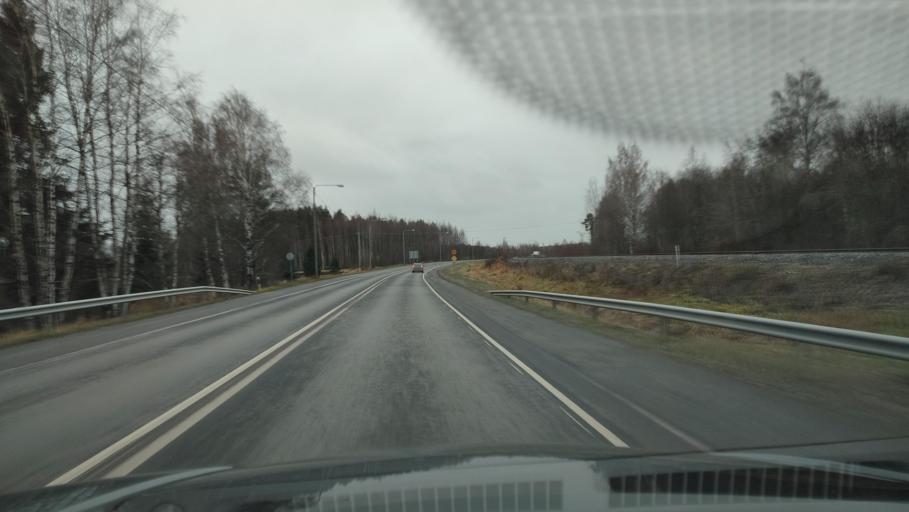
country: FI
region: Southern Ostrobothnia
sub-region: Seinaejoki
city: Ilmajoki
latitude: 62.7589
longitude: 22.6650
